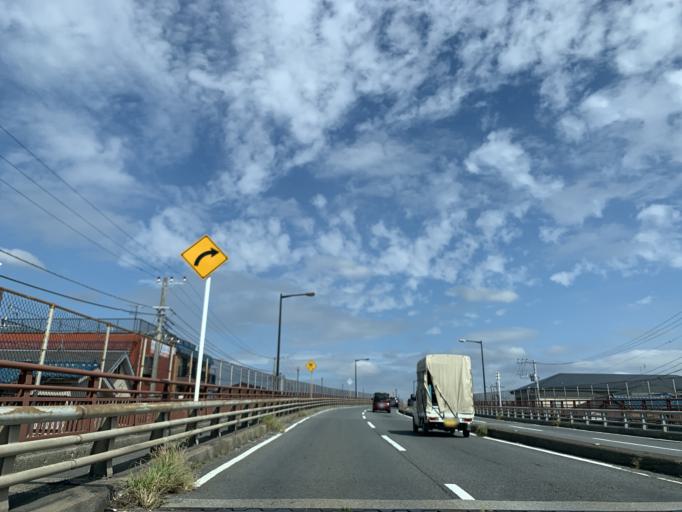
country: JP
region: Tokyo
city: Urayasu
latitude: 35.6990
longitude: 139.9239
